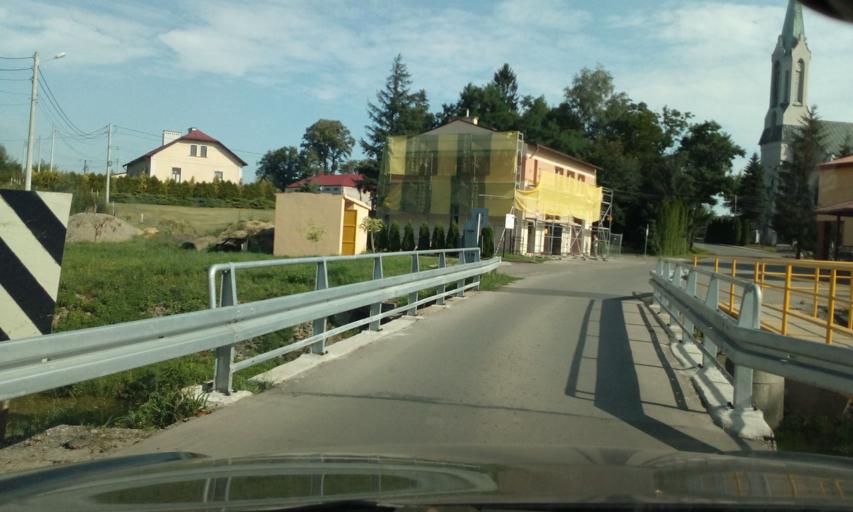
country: PL
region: Subcarpathian Voivodeship
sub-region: Powiat lancucki
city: Wysoka
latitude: 50.0437
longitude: 22.2492
